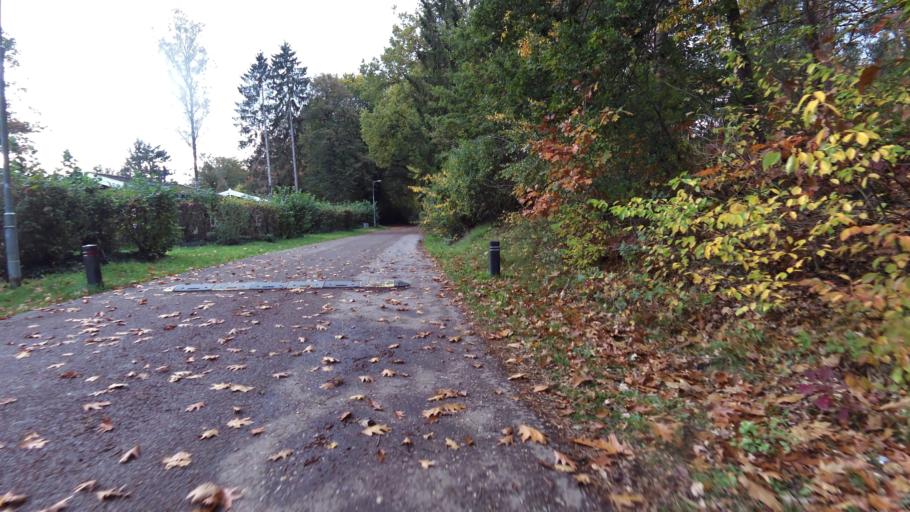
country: NL
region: Gelderland
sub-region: Gemeente Nunspeet
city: Nunspeet
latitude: 52.3293
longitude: 5.8211
